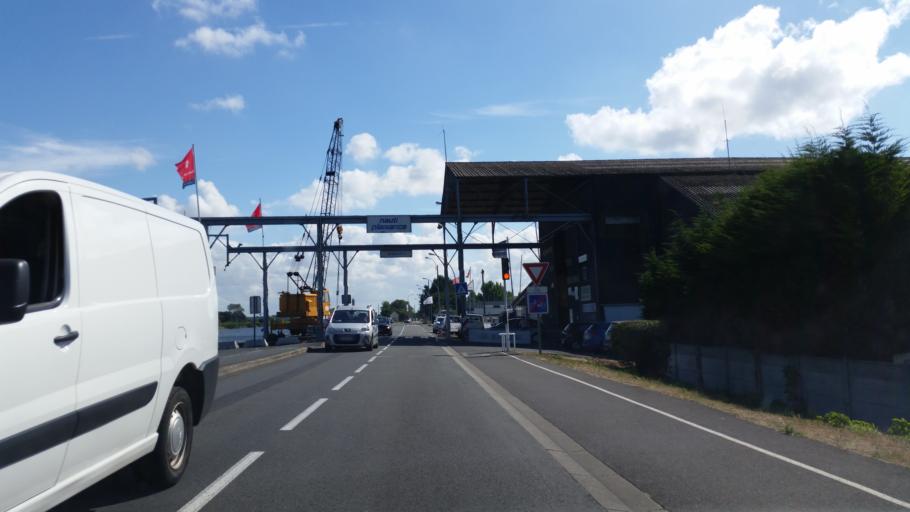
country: FR
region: Lower Normandy
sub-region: Departement du Calvados
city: Ouistreham
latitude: 49.2749
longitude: -0.2513
